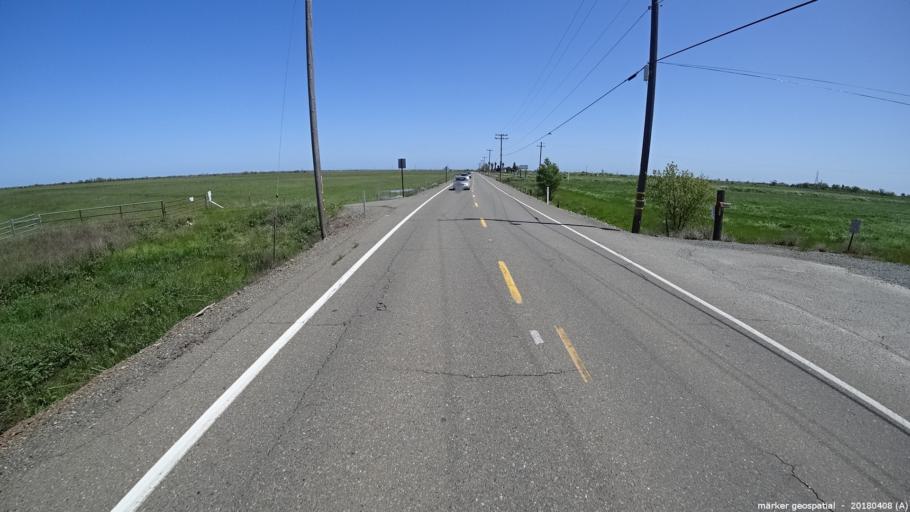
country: US
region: California
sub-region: Sacramento County
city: Laguna
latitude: 38.3696
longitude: -121.5009
